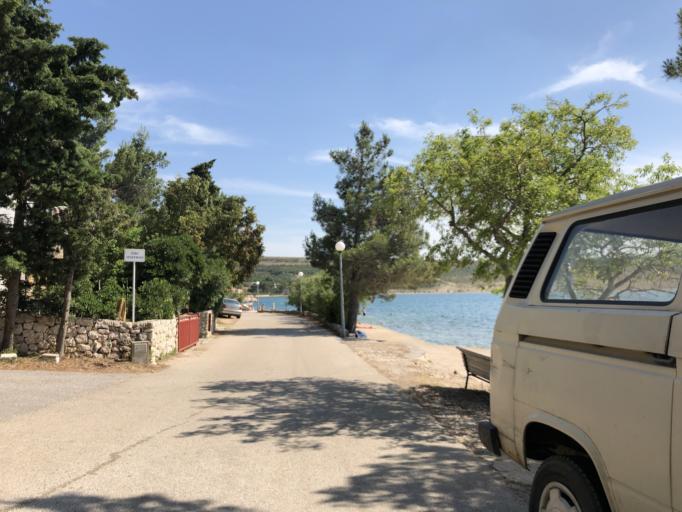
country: HR
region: Zadarska
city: Posedarje
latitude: 44.2518
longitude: 15.5368
